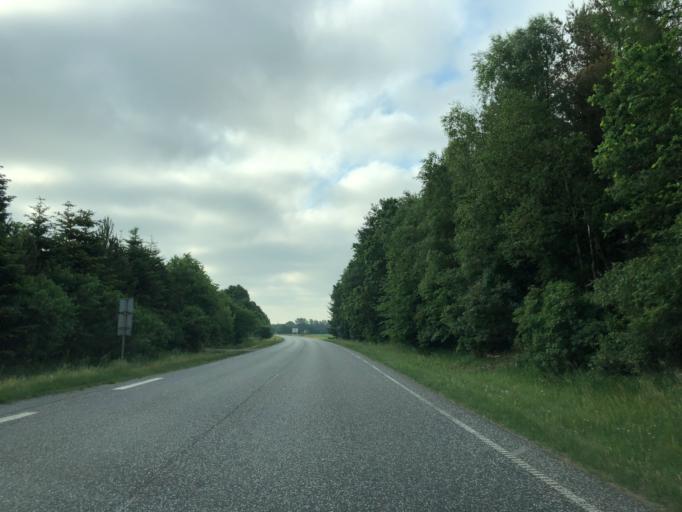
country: DK
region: South Denmark
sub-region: Vejle Kommune
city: Give
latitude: 55.7576
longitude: 9.3018
